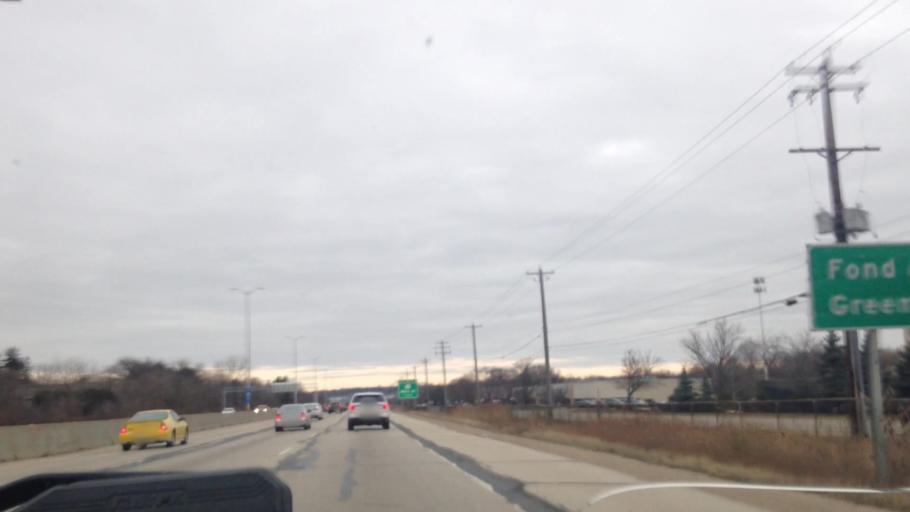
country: US
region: Wisconsin
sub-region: Waukesha County
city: Menomonee Falls
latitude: 43.1663
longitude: -88.0726
